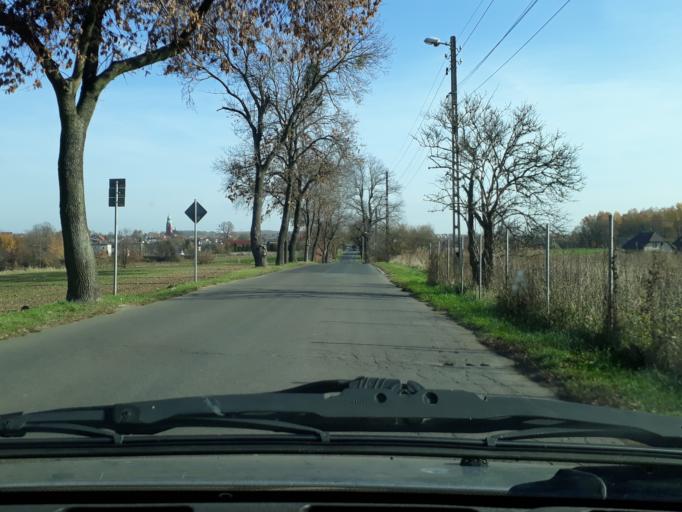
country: PL
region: Silesian Voivodeship
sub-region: Powiat tarnogorski
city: Tarnowskie Gory
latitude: 50.4248
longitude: 18.8534
